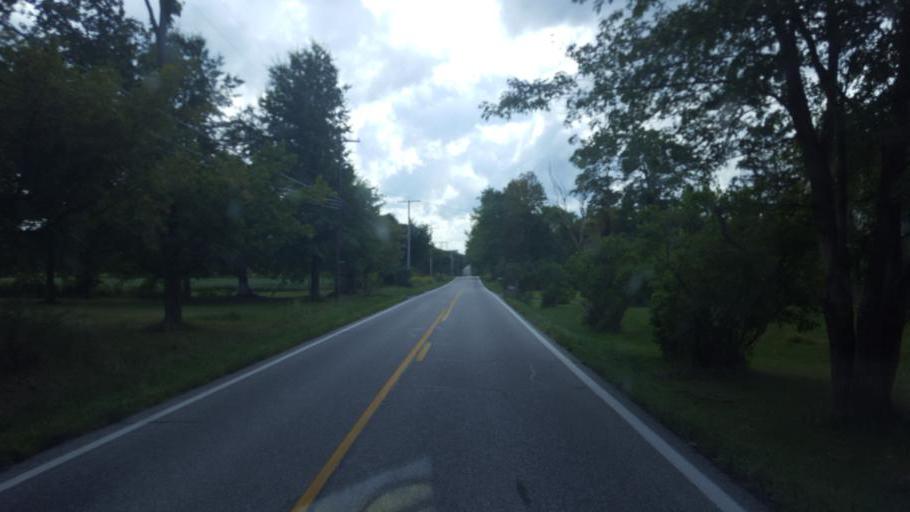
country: US
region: Ohio
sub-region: Geauga County
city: Burton
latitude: 41.4419
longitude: -81.1371
